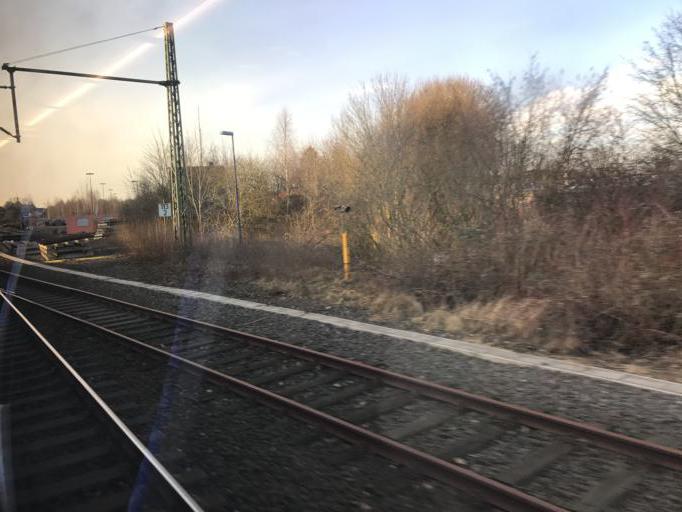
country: DE
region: Schleswig-Holstein
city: Rendsburg
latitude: 54.2979
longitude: 9.6776
